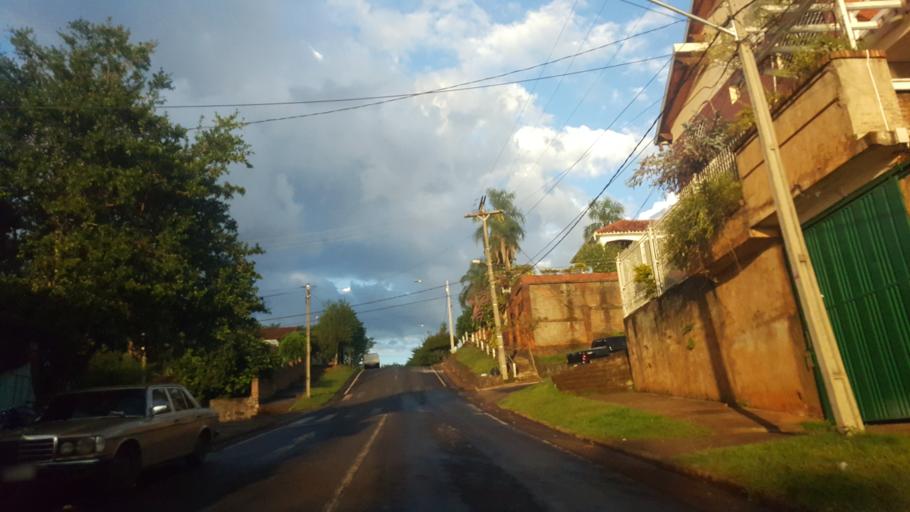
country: PY
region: Itapua
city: Encarnacion
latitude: -27.3627
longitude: -55.8606
